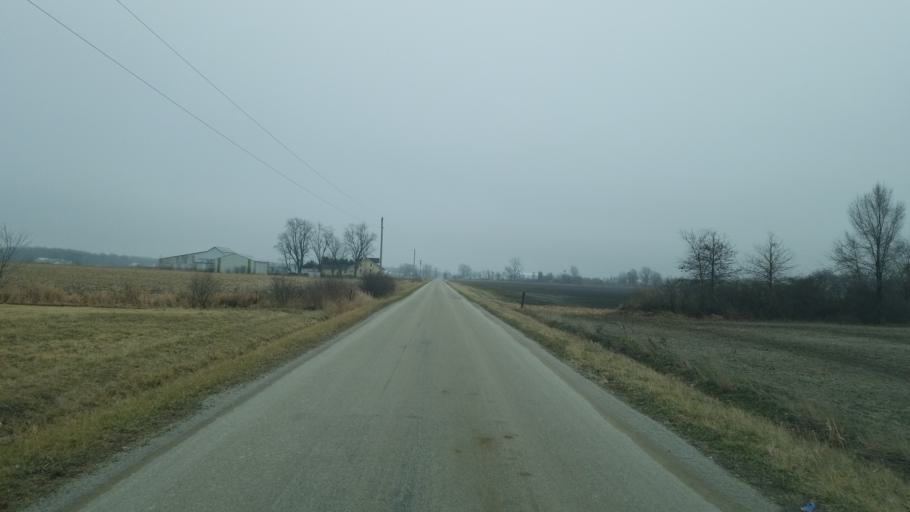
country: US
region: Indiana
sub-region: Adams County
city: Geneva
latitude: 40.5705
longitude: -84.9462
